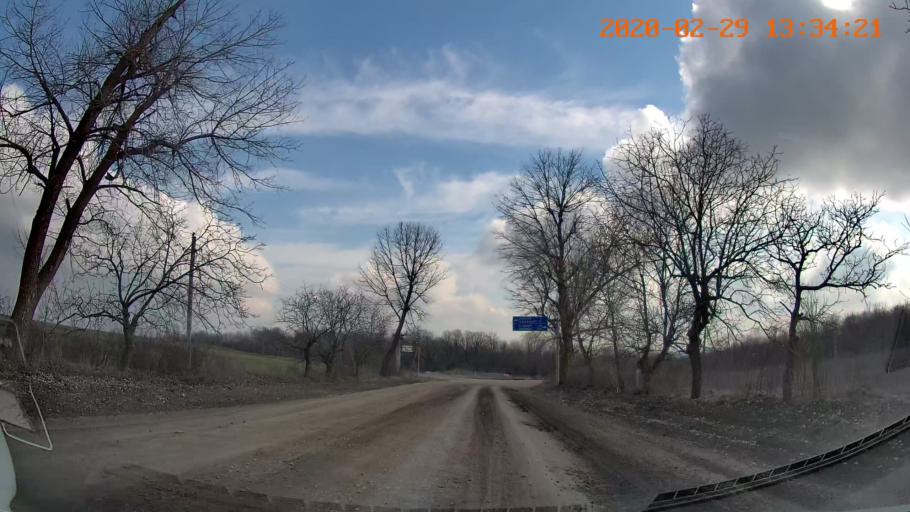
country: MD
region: Telenesti
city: Camenca
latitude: 47.8694
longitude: 28.6220
